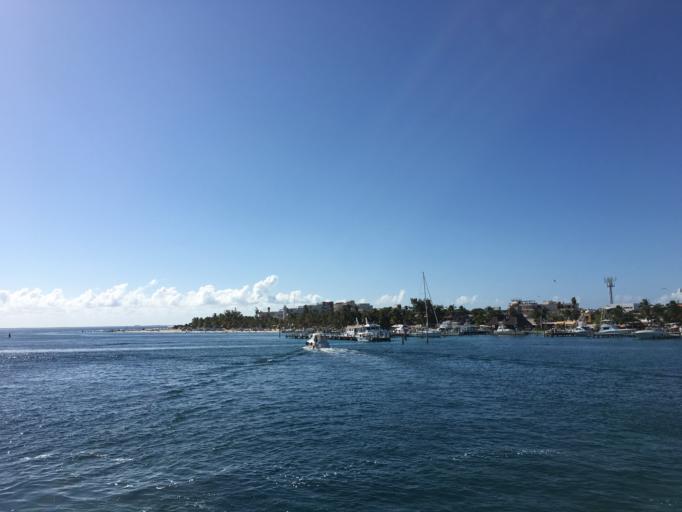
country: MX
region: Quintana Roo
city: Isla Mujeres
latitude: 21.2534
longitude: -86.7478
